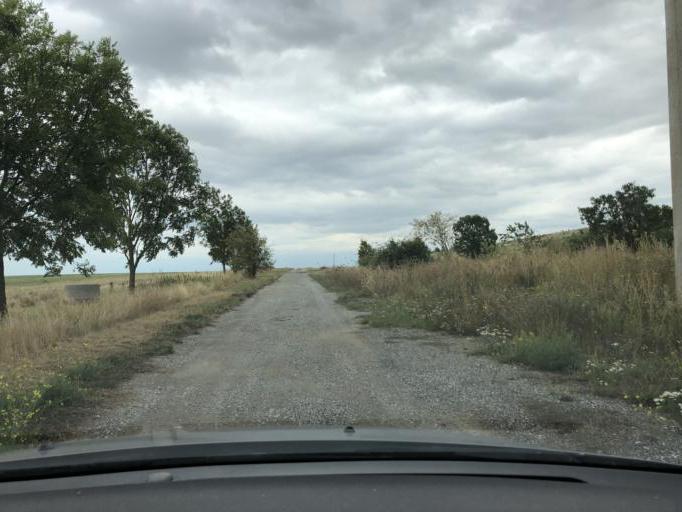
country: DE
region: Saxony-Anhalt
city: Nienburg/Saale
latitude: 51.8320
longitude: 11.7904
